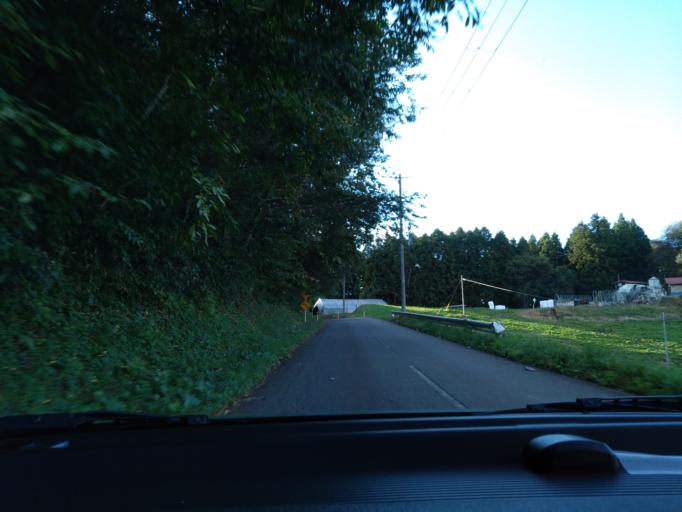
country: JP
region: Iwate
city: Ichinoseki
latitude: 38.8686
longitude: 141.1793
